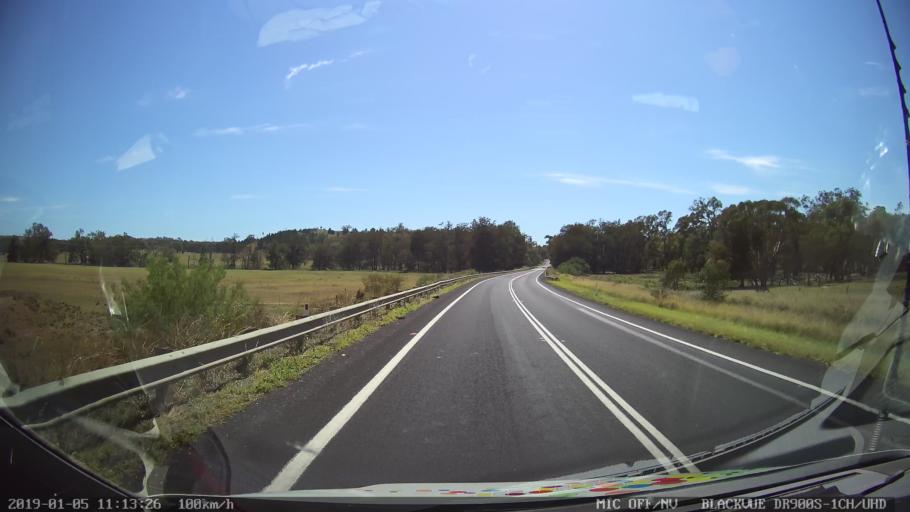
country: AU
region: New South Wales
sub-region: Warrumbungle Shire
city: Coonabarabran
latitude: -31.3706
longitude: 149.2705
